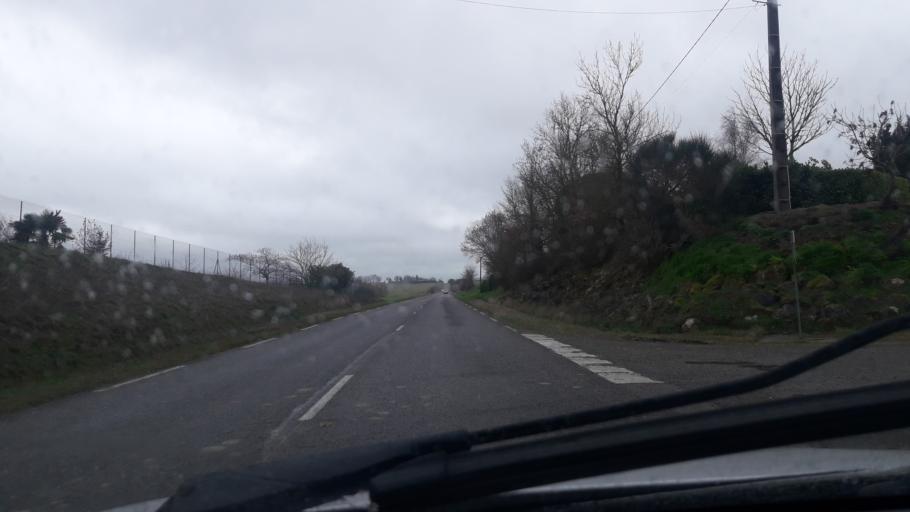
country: FR
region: Midi-Pyrenees
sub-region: Departement du Gers
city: Gimont
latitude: 43.7134
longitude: 0.9861
